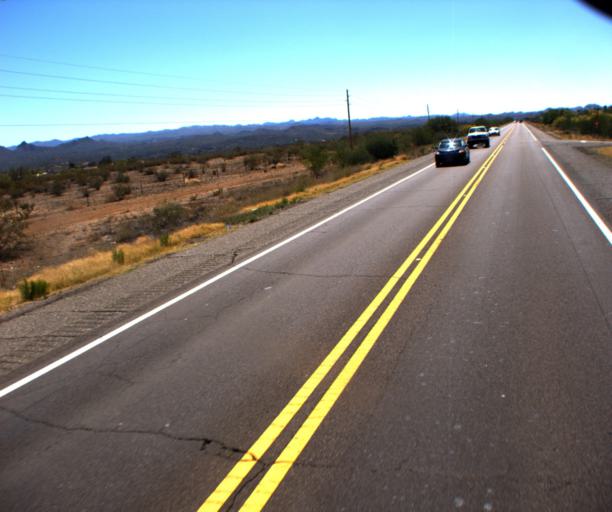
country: US
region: Arizona
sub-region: Maricopa County
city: Wickenburg
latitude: 34.0101
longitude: -112.7861
